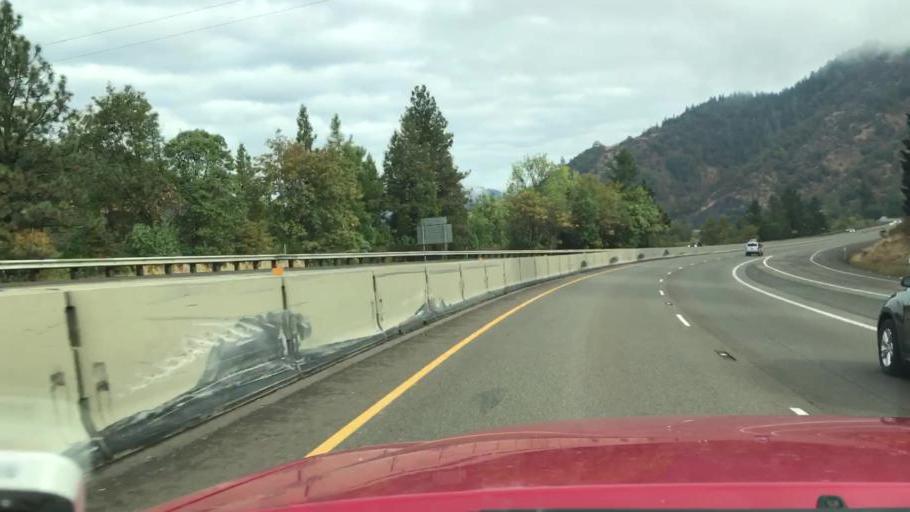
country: US
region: Oregon
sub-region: Douglas County
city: Riddle
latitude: 42.9495
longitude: -123.3315
